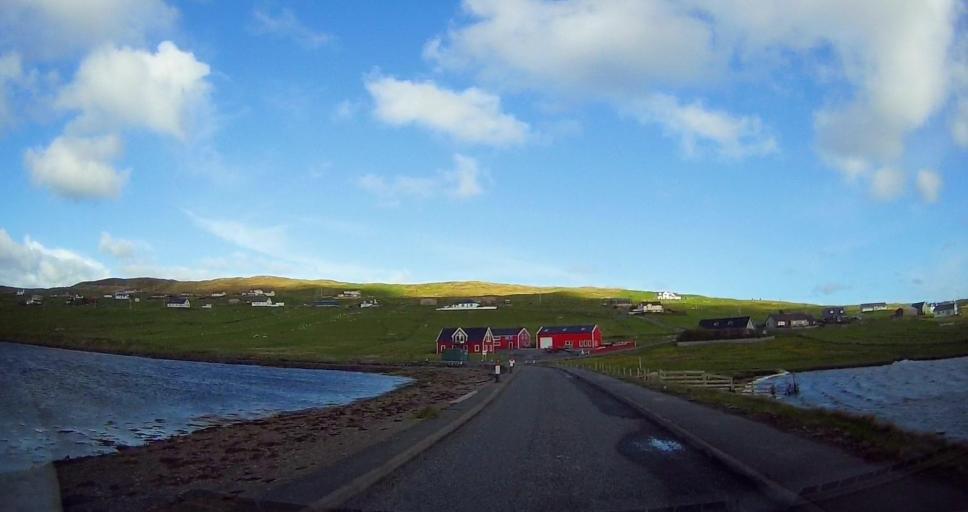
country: GB
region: Scotland
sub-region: Shetland Islands
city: Shetland
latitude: 60.3697
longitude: -1.1314
